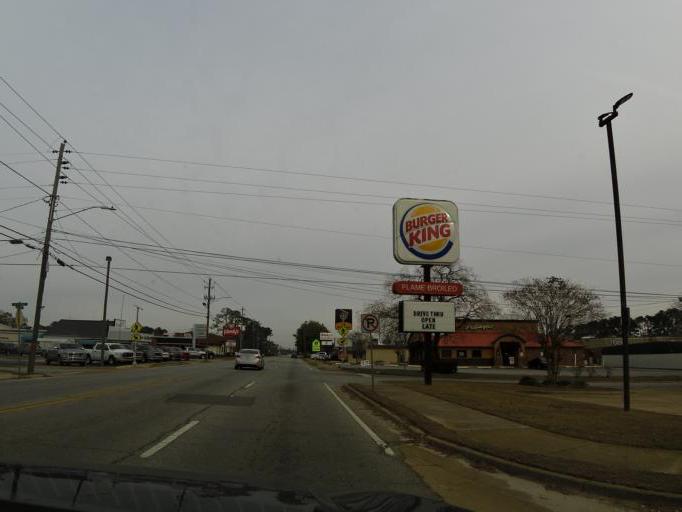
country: US
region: Georgia
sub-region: Decatur County
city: Bainbridge
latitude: 30.9039
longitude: -84.5583
